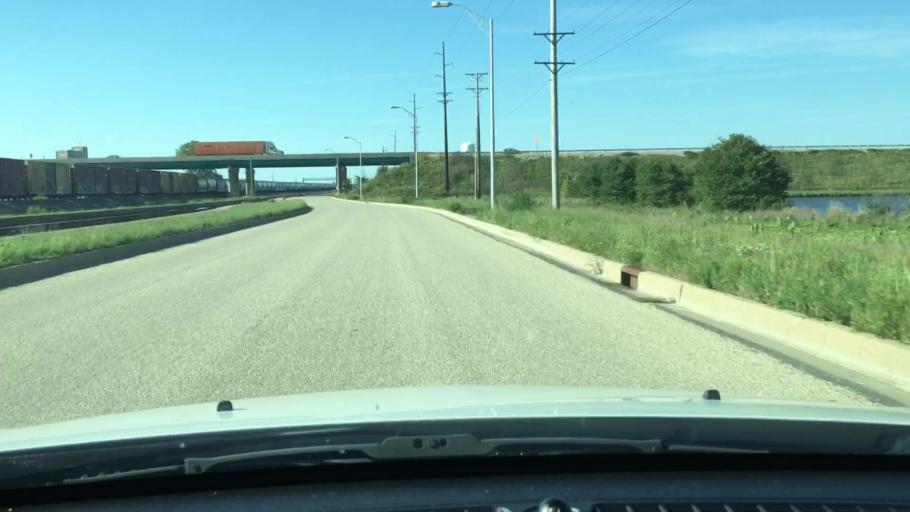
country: US
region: Illinois
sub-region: Ogle County
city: Rochelle
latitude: 41.9006
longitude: -89.0428
